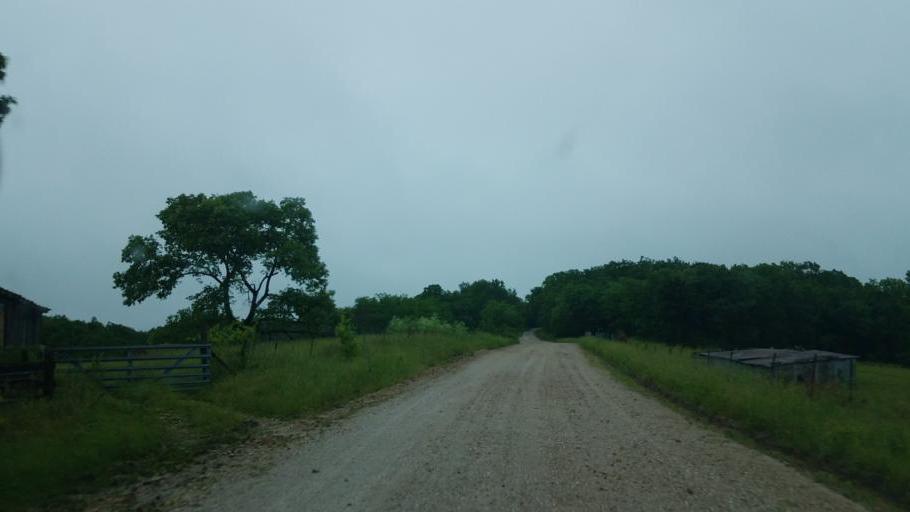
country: US
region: Missouri
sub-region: Moniteau County
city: California
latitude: 38.7390
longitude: -92.6082
